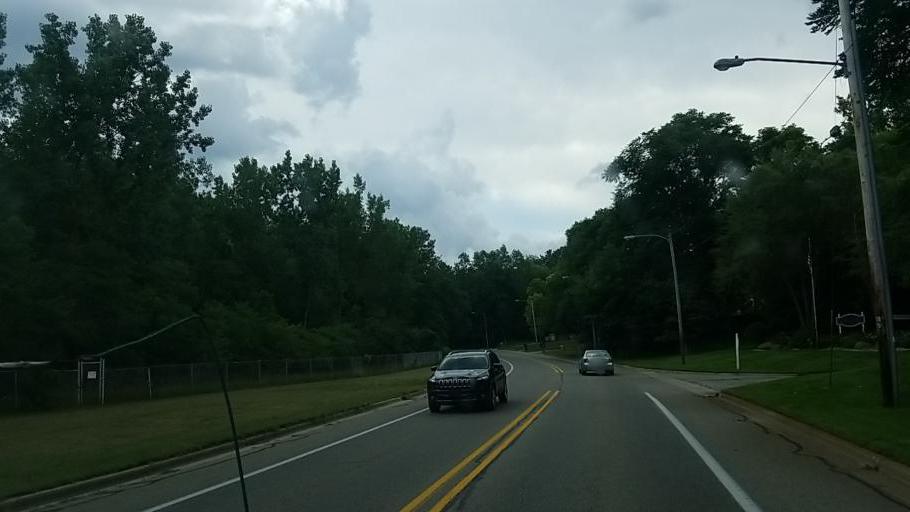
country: US
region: Michigan
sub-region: Kent County
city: Walker
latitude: 42.9992
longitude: -85.7184
